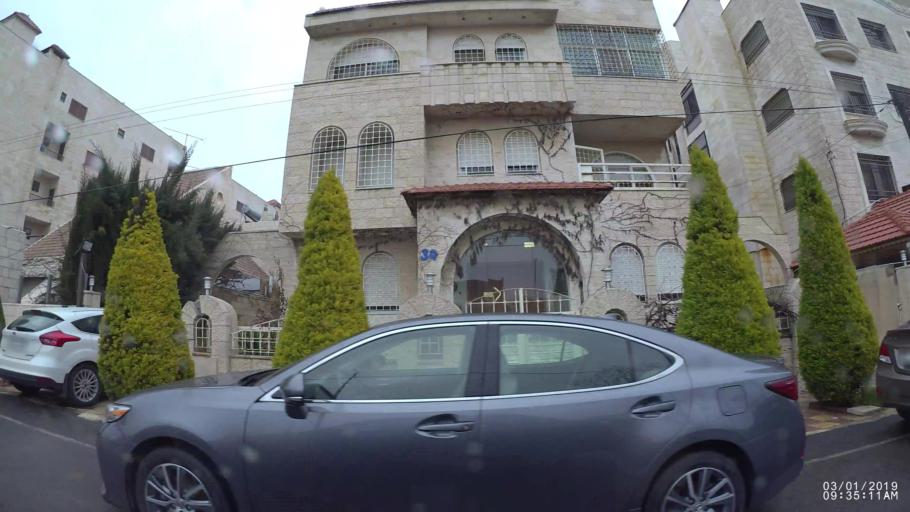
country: JO
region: Amman
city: Wadi as Sir
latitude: 31.9718
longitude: 35.8408
